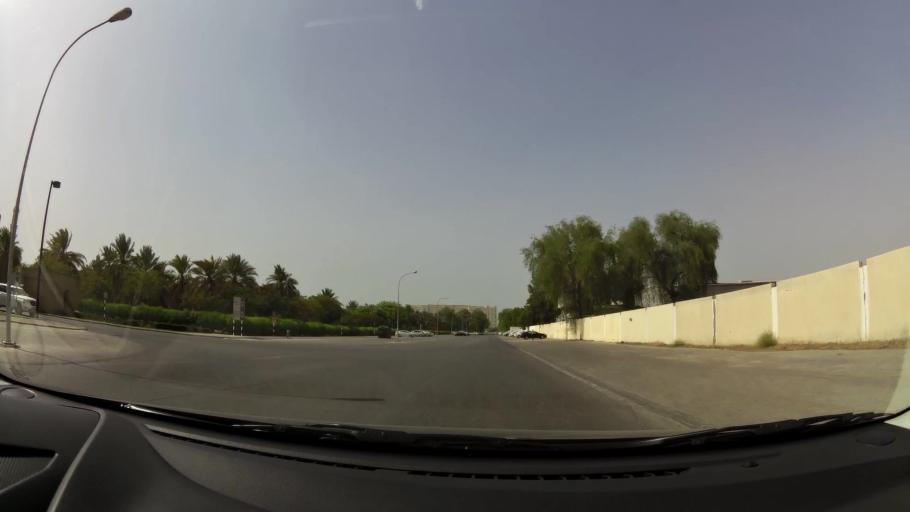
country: OM
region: Muhafazat Masqat
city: Bawshar
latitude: 23.5817
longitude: 58.3920
